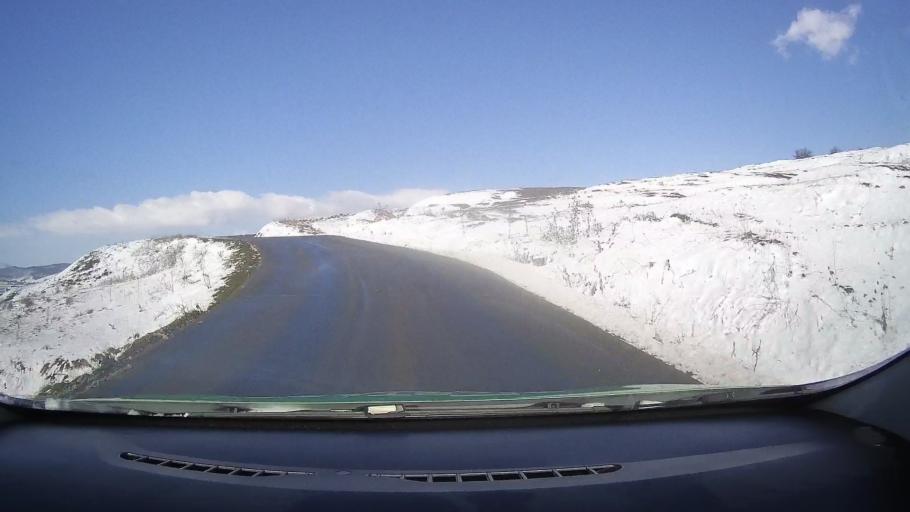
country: RO
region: Sibiu
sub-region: Comuna Rosia
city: Rosia
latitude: 45.8043
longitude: 24.2914
